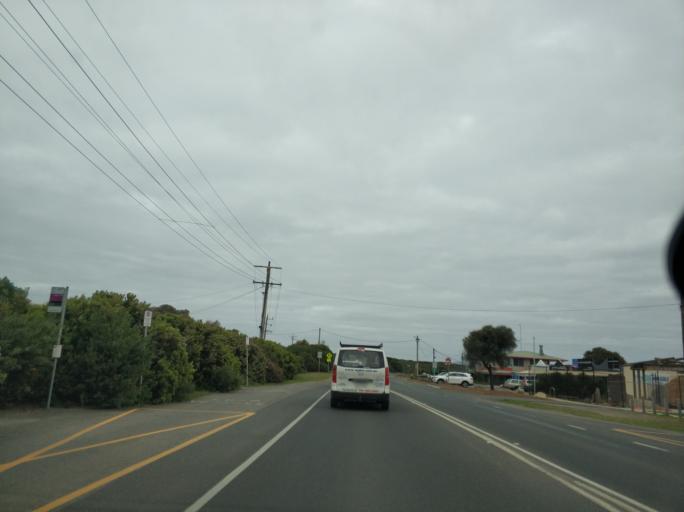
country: AU
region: Victoria
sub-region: Surf Coast
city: Anglesea
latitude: -38.4646
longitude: 144.1003
